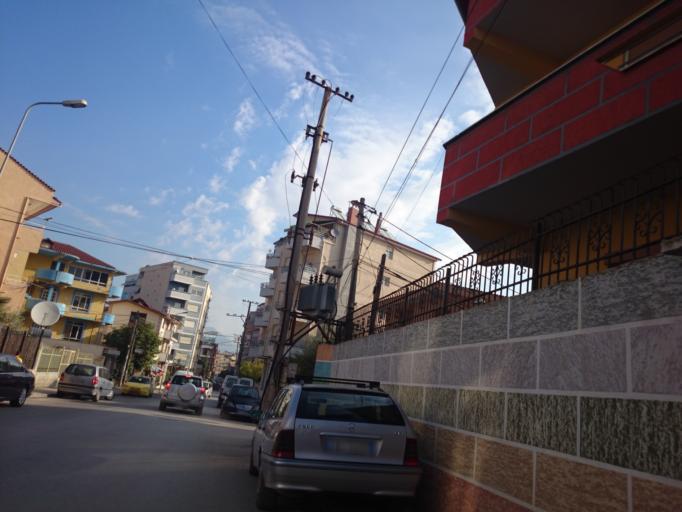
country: AL
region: Tirane
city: Tirana
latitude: 41.3171
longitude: 19.7986
